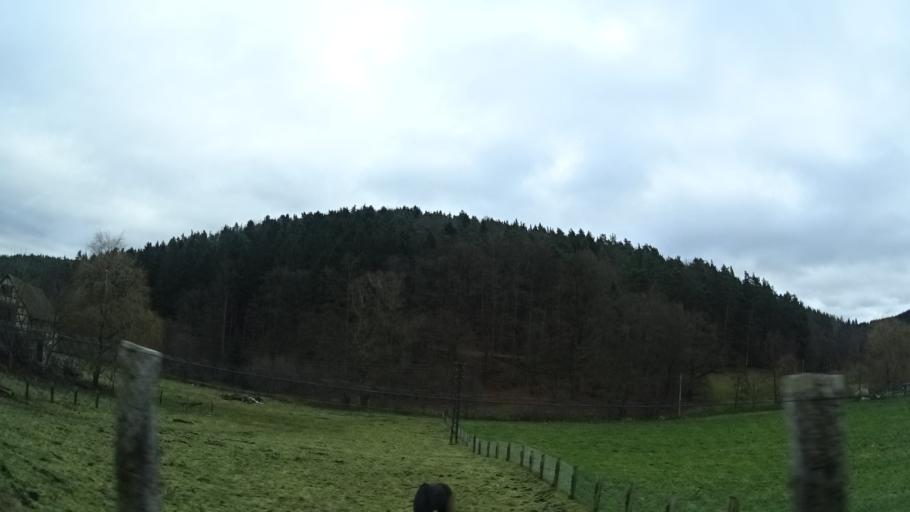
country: DE
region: Thuringia
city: Herschdorf
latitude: 50.7178
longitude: 11.4981
